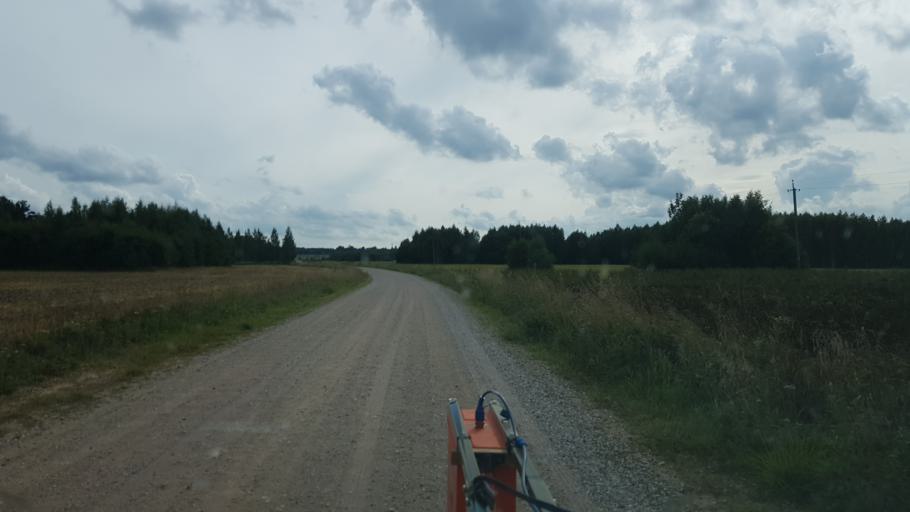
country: RU
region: Pskov
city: Pechory
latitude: 57.8125
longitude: 27.5128
